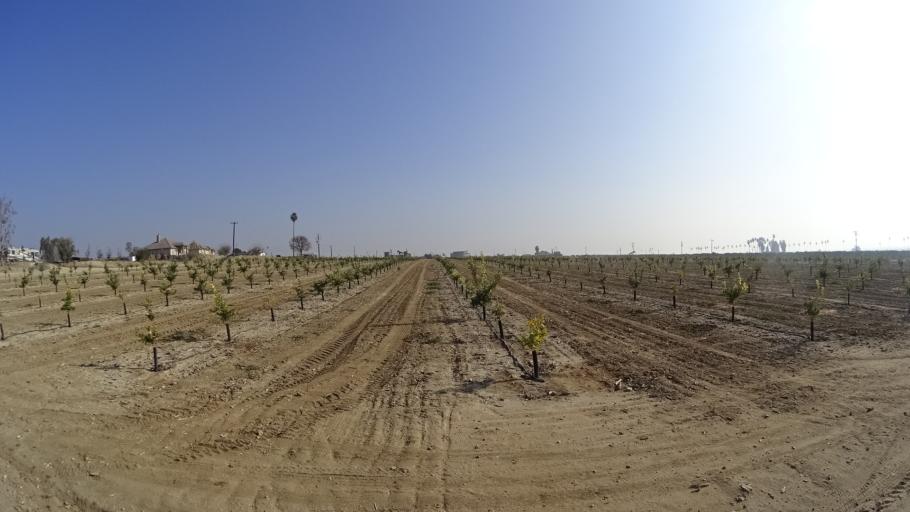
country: US
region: California
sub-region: Kern County
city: Lamont
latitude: 35.3631
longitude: -118.8787
